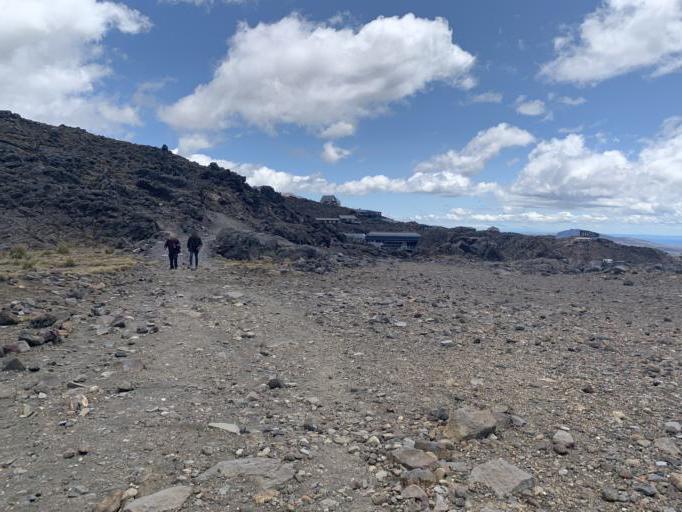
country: NZ
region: Manawatu-Wanganui
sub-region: Ruapehu District
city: Waiouru
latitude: -39.2365
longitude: 175.5602
